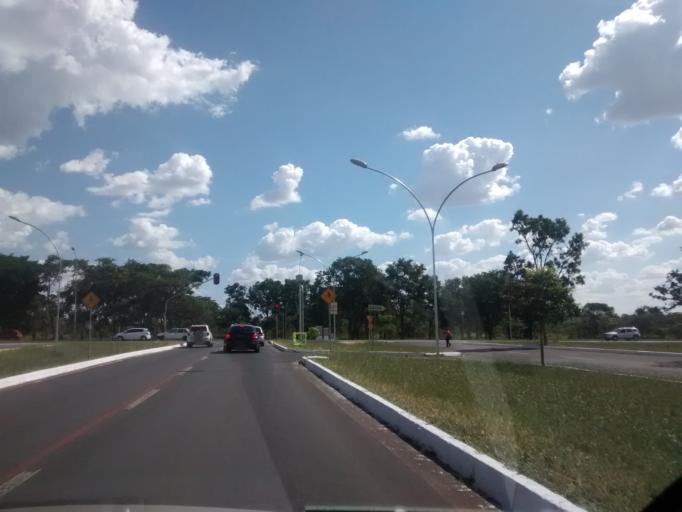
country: BR
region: Federal District
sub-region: Brasilia
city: Brasilia
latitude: -15.7807
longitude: -47.9249
